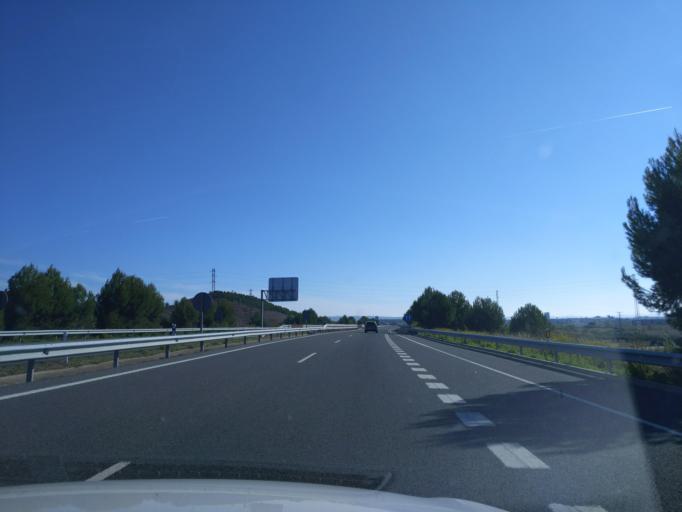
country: ES
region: Navarre
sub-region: Provincia de Navarra
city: Viana
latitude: 42.4756
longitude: -2.3481
